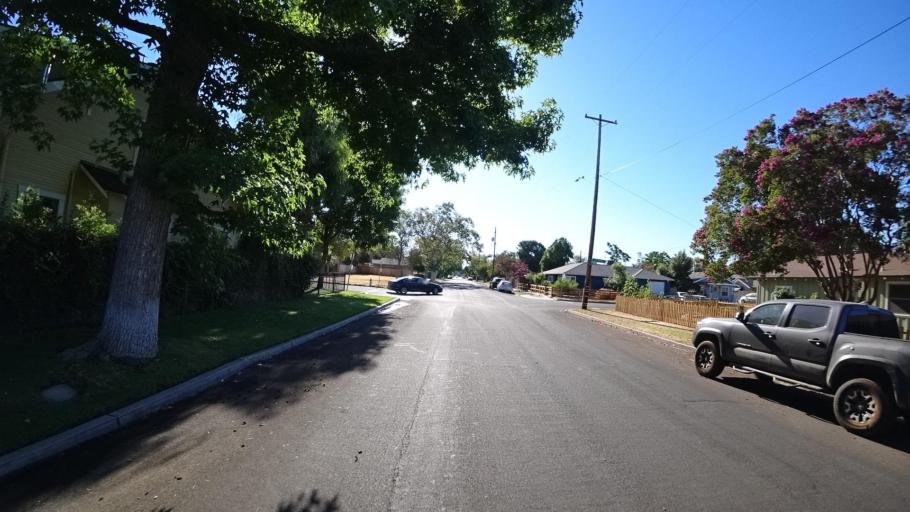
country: US
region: California
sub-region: Fresno County
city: Fresno
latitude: 36.7614
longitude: -119.7948
